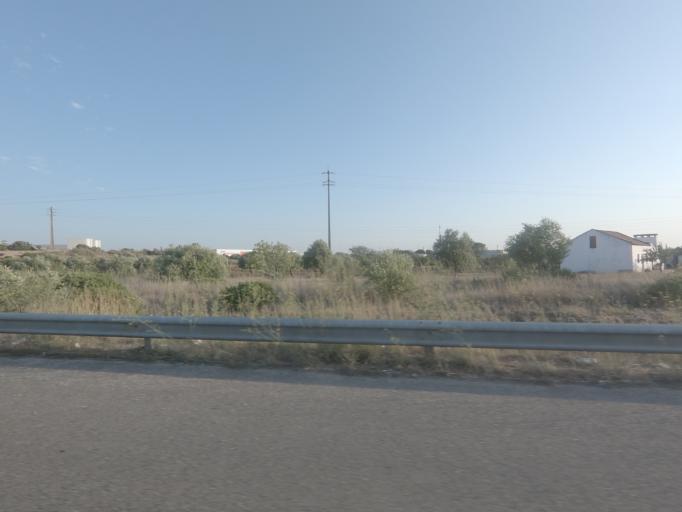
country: PT
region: Santarem
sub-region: Alcanena
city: Alcanena
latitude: 39.4818
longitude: -8.6261
